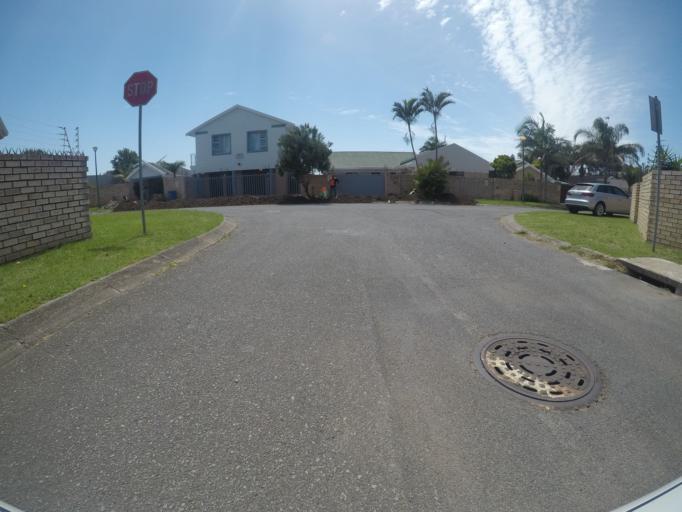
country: ZA
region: Eastern Cape
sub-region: Buffalo City Metropolitan Municipality
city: East London
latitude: -32.9510
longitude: 28.0005
